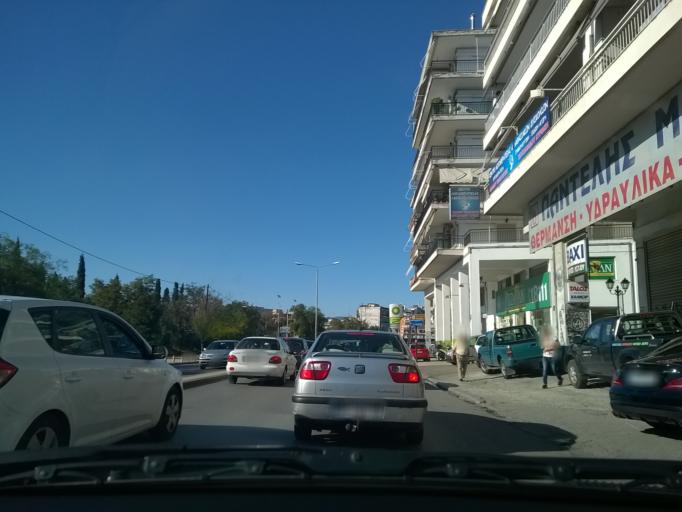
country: GR
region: Central Macedonia
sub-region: Nomos Thessalonikis
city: Ampelokipoi
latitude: 40.6551
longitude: 22.9346
